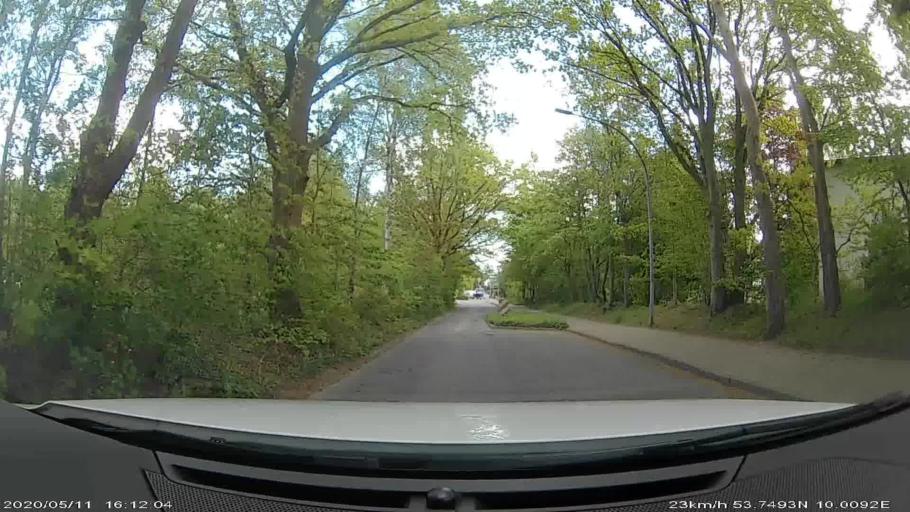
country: DE
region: Schleswig-Holstein
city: Henstedt-Ulzburg
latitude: 53.7507
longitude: 10.0057
